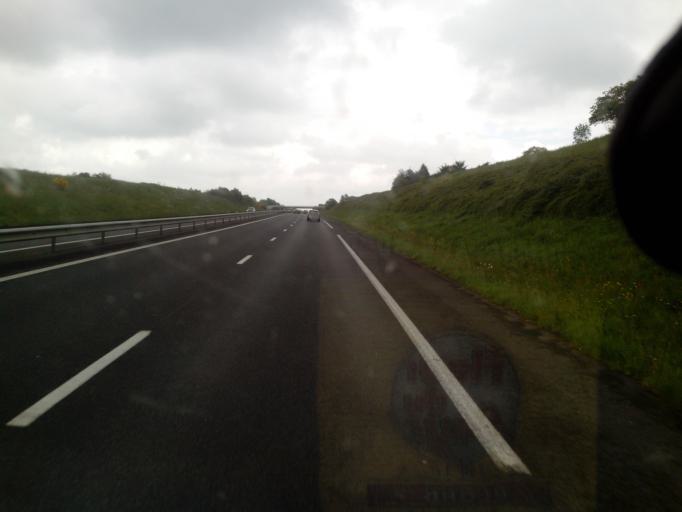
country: FR
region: Lower Normandy
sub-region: Departement de la Manche
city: Saint-Amand
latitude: 48.9971
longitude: -0.9144
